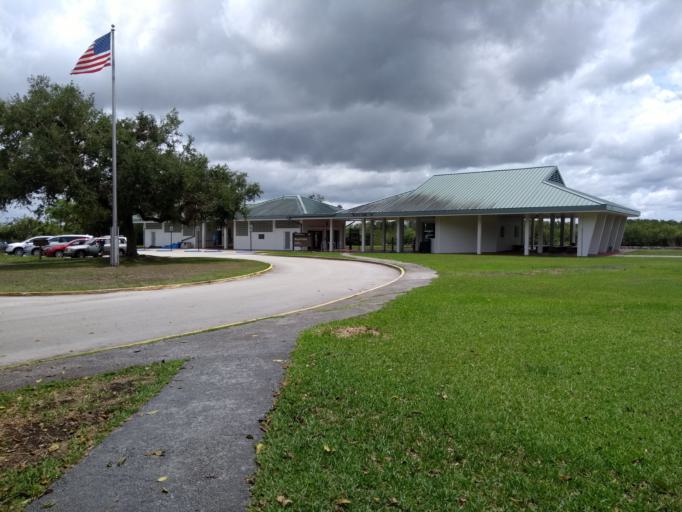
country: US
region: Florida
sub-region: Miami-Dade County
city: Florida City
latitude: 25.3822
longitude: -80.6101
